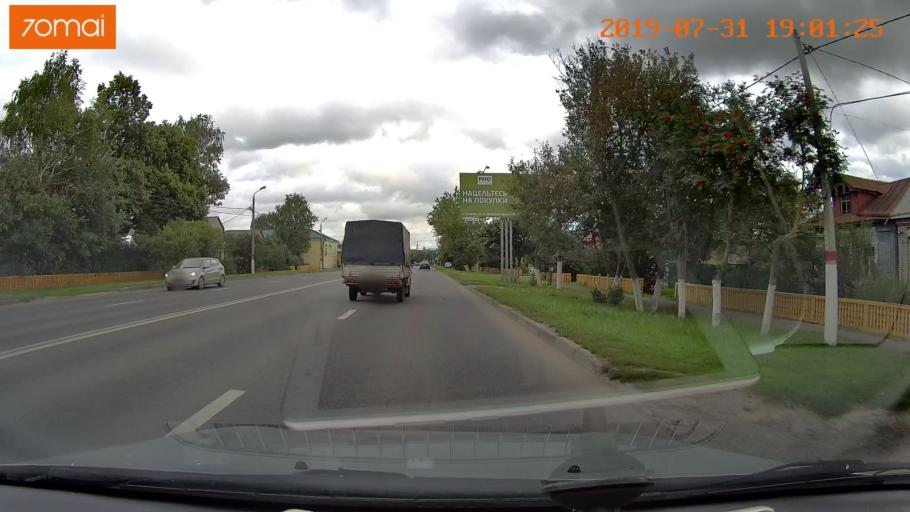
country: RU
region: Moskovskaya
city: Raduzhnyy
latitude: 55.1267
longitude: 38.7288
